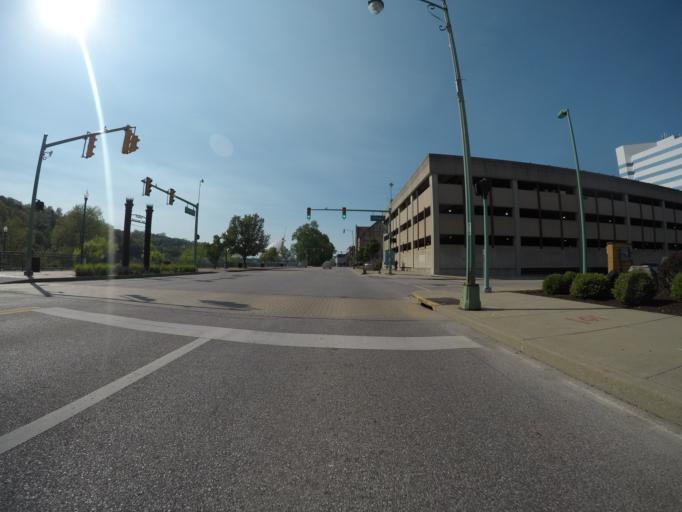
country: US
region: West Virginia
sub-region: Kanawha County
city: Charleston
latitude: 38.3498
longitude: -81.6384
